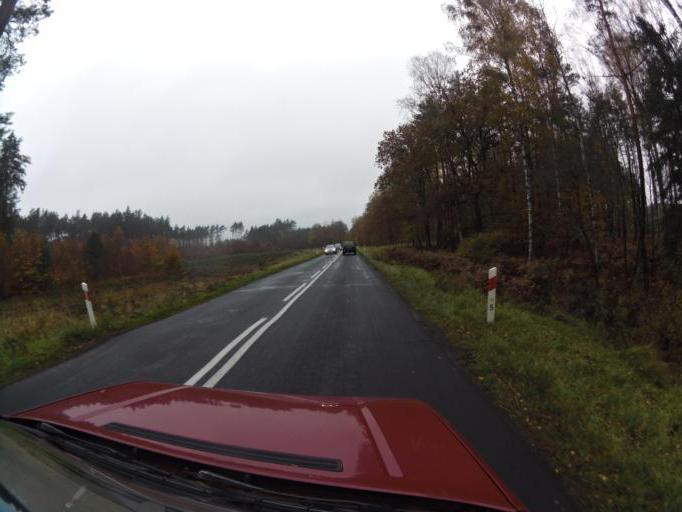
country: PL
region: West Pomeranian Voivodeship
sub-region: Powiat policki
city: Dobra
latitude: 53.5789
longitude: 14.4263
